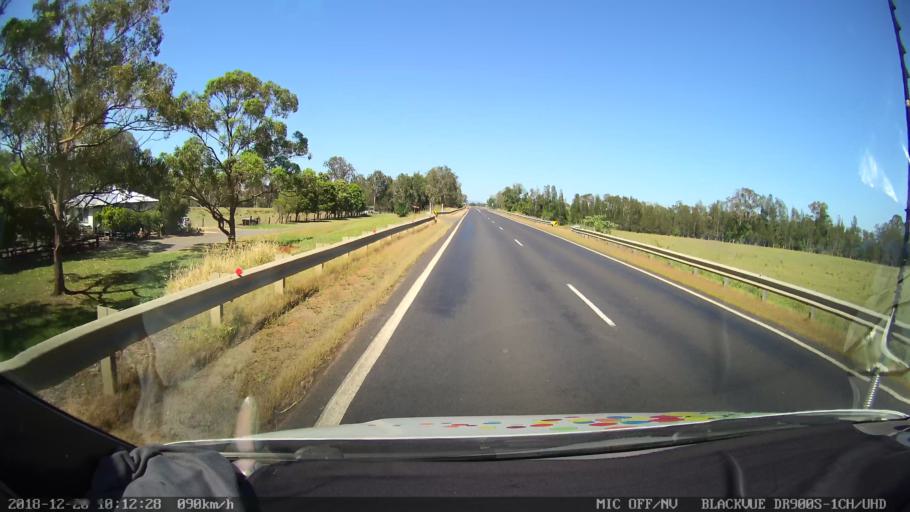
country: AU
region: New South Wales
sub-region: Richmond Valley
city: Casino
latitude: -28.8733
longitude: 153.1436
